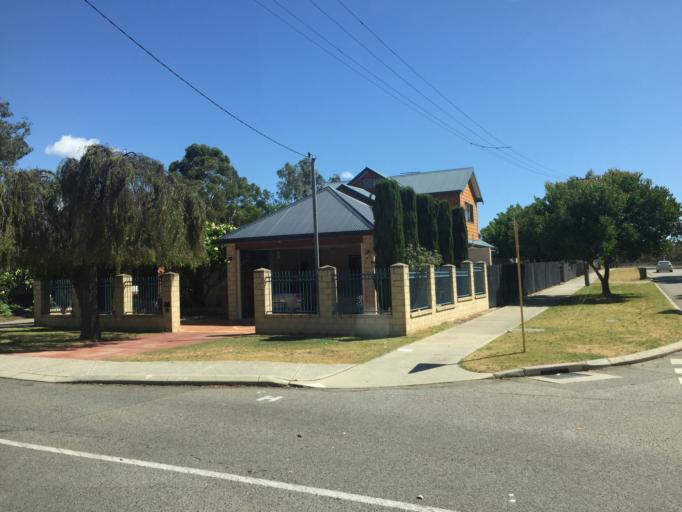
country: AU
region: Western Australia
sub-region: Belmont
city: Redcliffe
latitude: -31.9330
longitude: 115.9454
